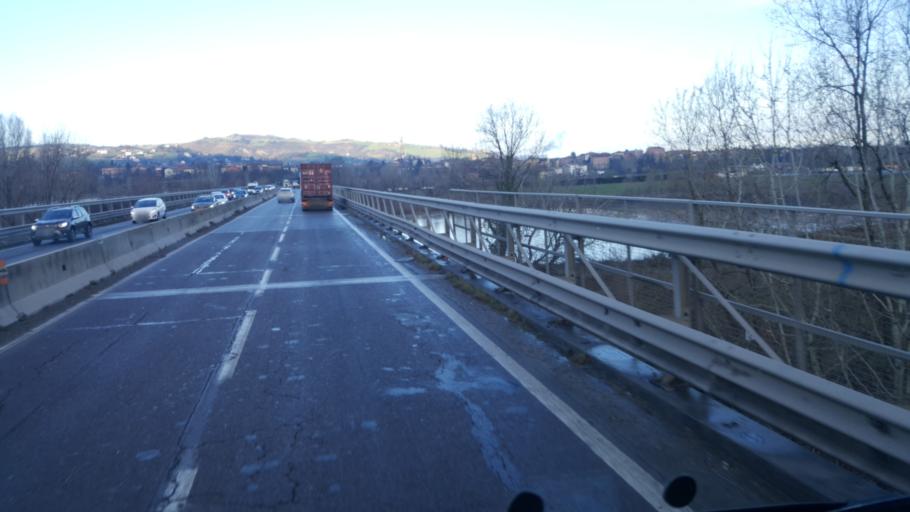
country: IT
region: Emilia-Romagna
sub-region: Provincia di Modena
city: Sassuolo
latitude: 44.5592
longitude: 10.7755
